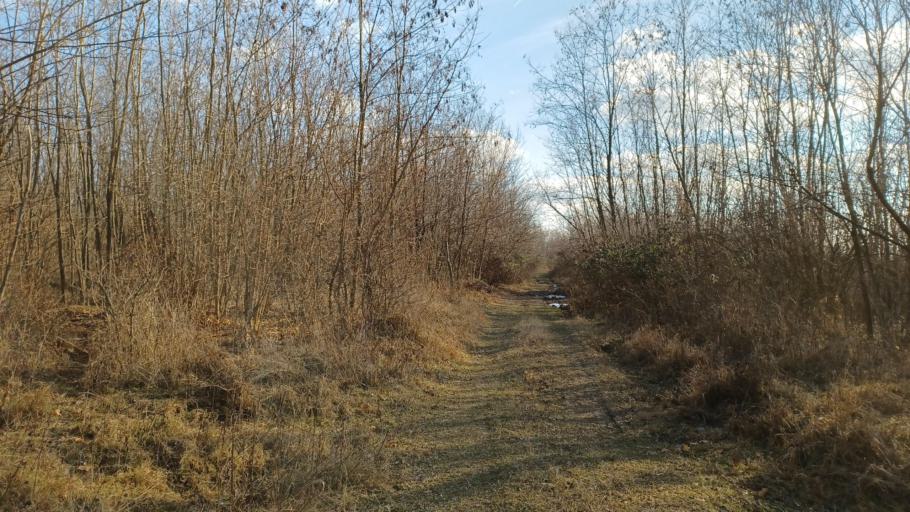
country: HU
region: Tolna
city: Szentgalpuszta
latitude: 46.3256
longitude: 18.6137
